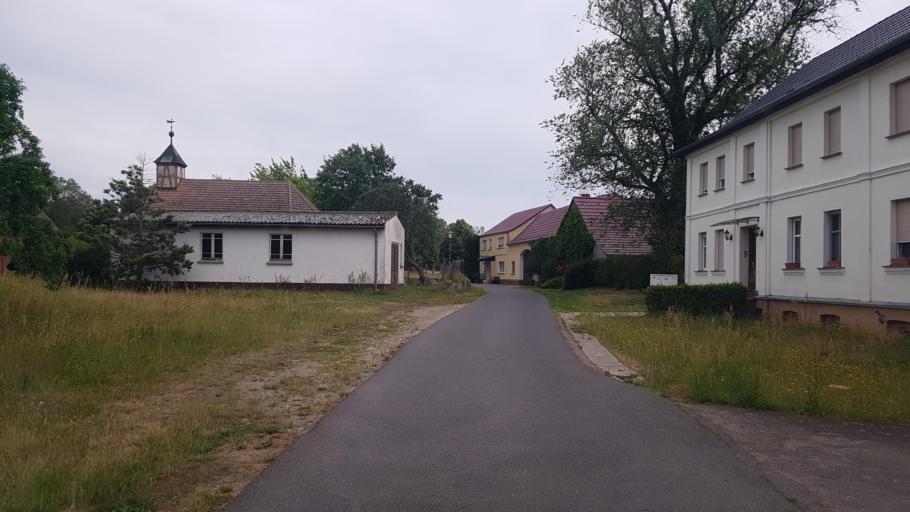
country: DE
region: Saxony-Anhalt
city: Kropstadt
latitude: 52.0130
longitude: 12.7912
